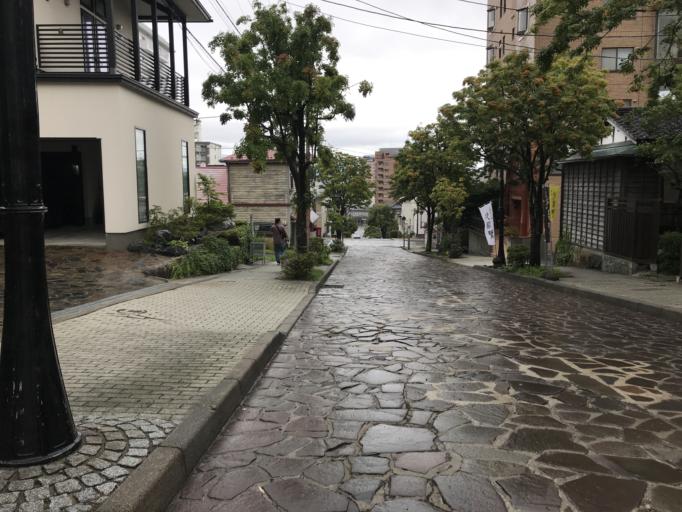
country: JP
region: Hokkaido
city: Hakodate
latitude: 41.7638
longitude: 140.7140
